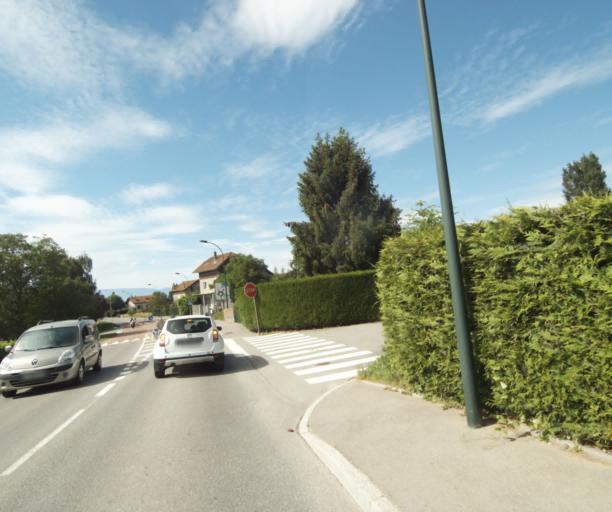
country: FR
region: Rhone-Alpes
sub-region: Departement de la Haute-Savoie
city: Thonon-les-Bains
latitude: 46.3510
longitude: 6.4787
